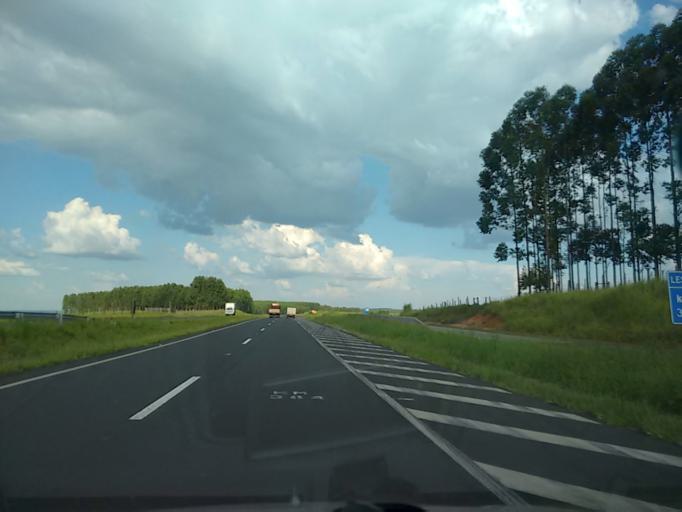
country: BR
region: Sao Paulo
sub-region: Duartina
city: Duartina
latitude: -22.3245
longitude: -49.4042
